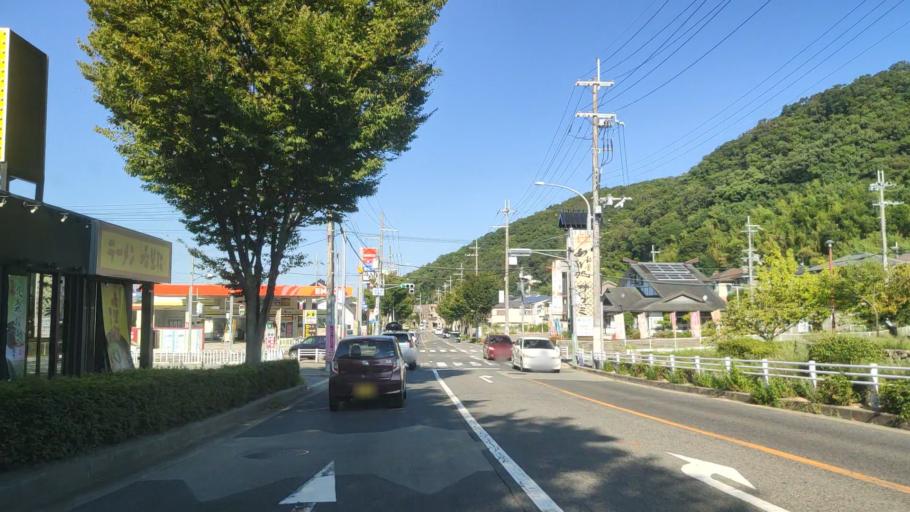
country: JP
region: Hyogo
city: Kobe
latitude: 34.7608
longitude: 135.1654
